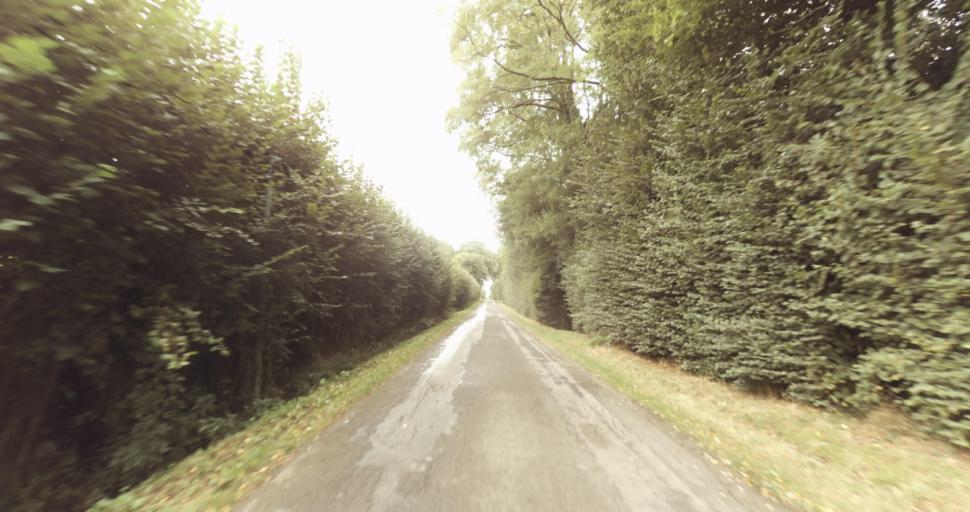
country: FR
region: Lower Normandy
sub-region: Departement de l'Orne
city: Sainte-Gauburge-Sainte-Colombe
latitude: 48.7053
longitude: 0.4471
